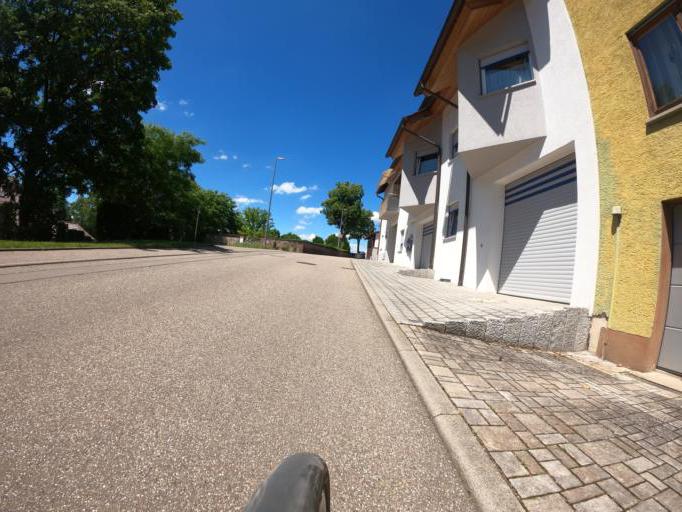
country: DE
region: Baden-Wuerttemberg
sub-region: Regierungsbezirk Stuttgart
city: Sersheim
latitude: 48.9635
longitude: 9.0145
